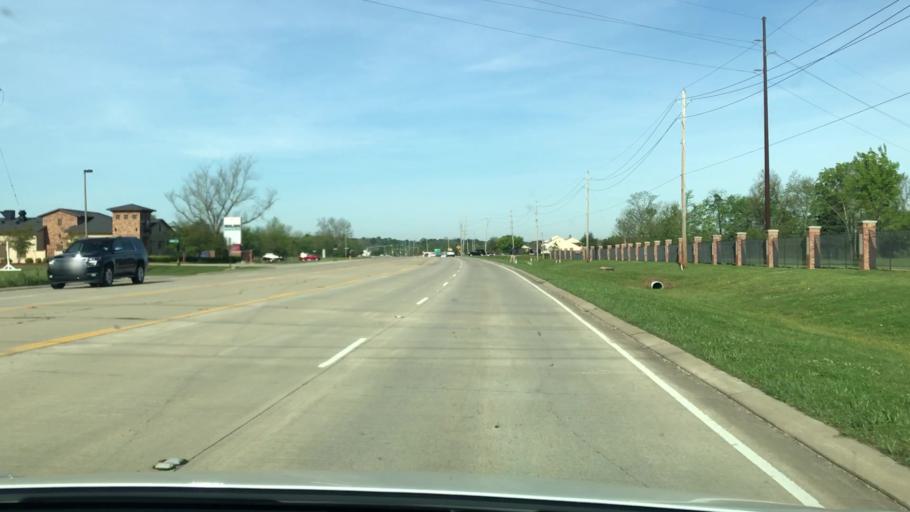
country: US
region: Louisiana
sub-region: Bossier Parish
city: Bossier City
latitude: 32.4012
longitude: -93.7085
